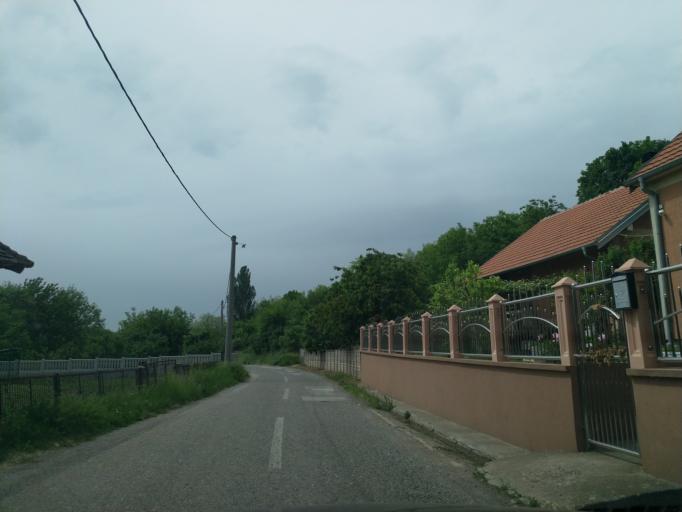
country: RS
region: Central Serbia
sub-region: Pomoravski Okrug
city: Paracin
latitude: 43.8633
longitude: 21.5855
